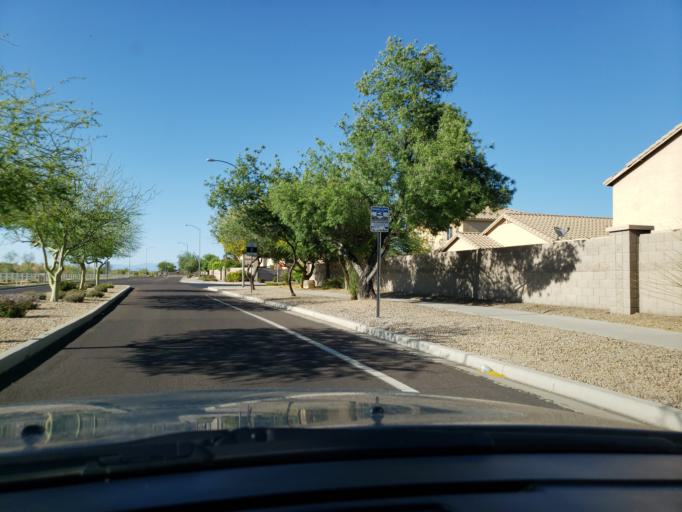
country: US
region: Arizona
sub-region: Maricopa County
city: Youngtown
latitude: 33.5756
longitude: -112.3113
